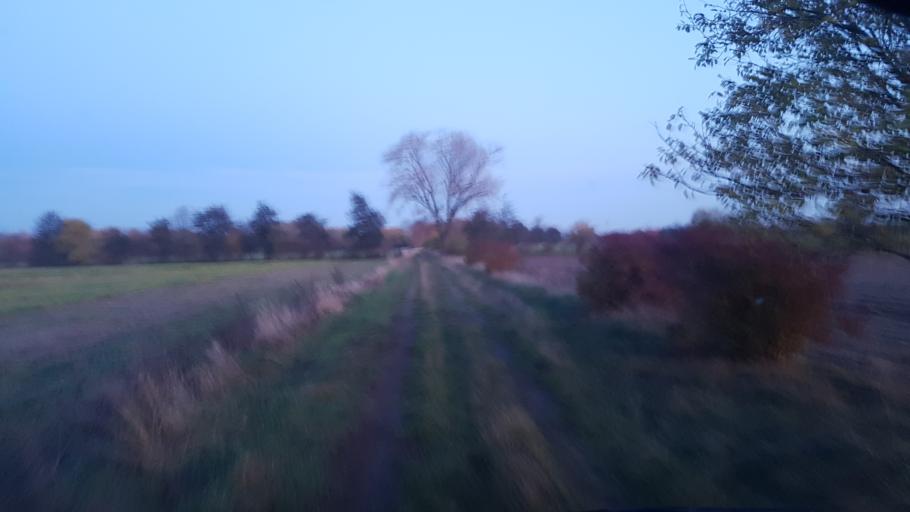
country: DE
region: Brandenburg
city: Schilda
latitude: 51.6204
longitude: 13.3470
